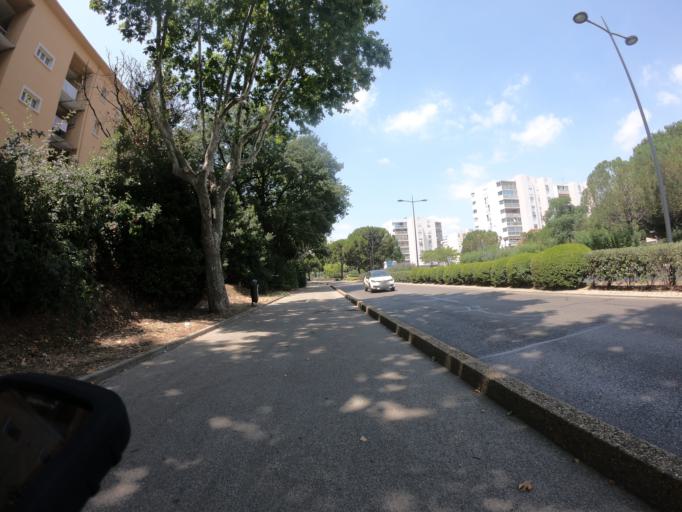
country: FR
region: Provence-Alpes-Cote d'Azur
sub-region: Departement du Var
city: Six-Fours-les-Plages
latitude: 43.1078
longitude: 5.8671
